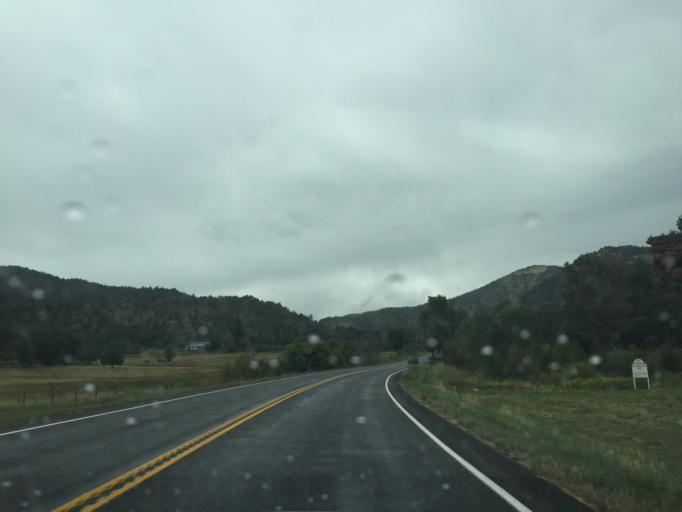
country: US
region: Utah
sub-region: Kane County
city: Kanab
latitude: 37.3416
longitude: -112.6049
